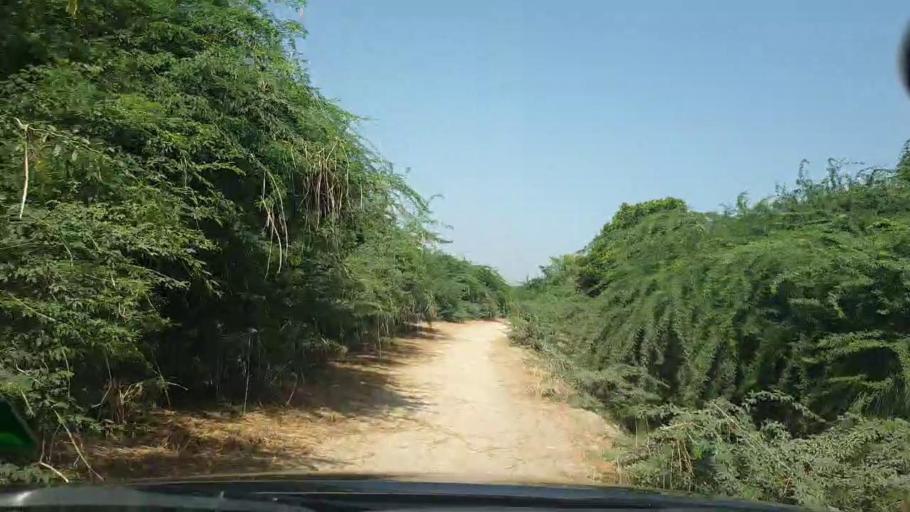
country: PK
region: Sindh
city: Tando Bago
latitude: 24.7727
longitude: 68.9489
